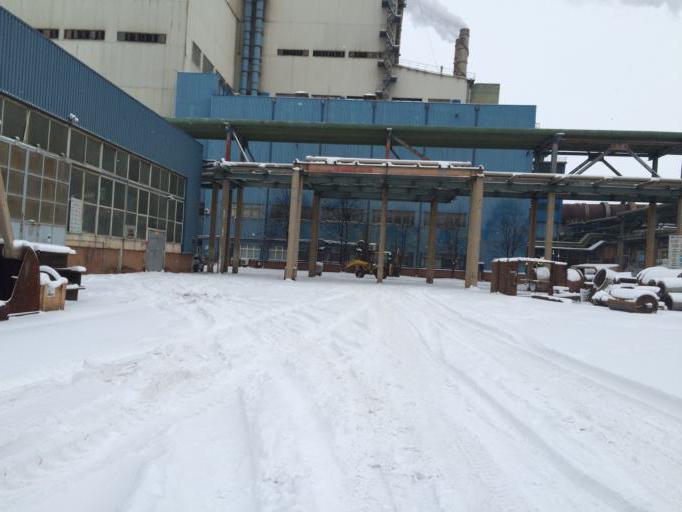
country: XK
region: Pristina
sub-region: Komuna e Drenasit
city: Glogovac
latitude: 42.6417
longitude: 20.9007
